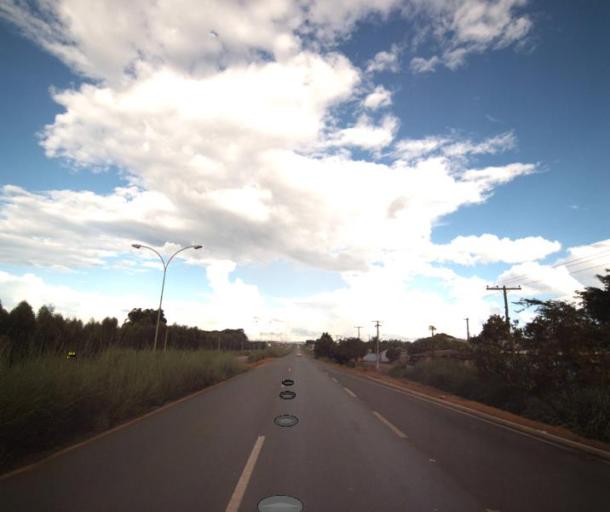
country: BR
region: Goias
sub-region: Anapolis
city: Anapolis
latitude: -16.2837
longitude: -48.9533
